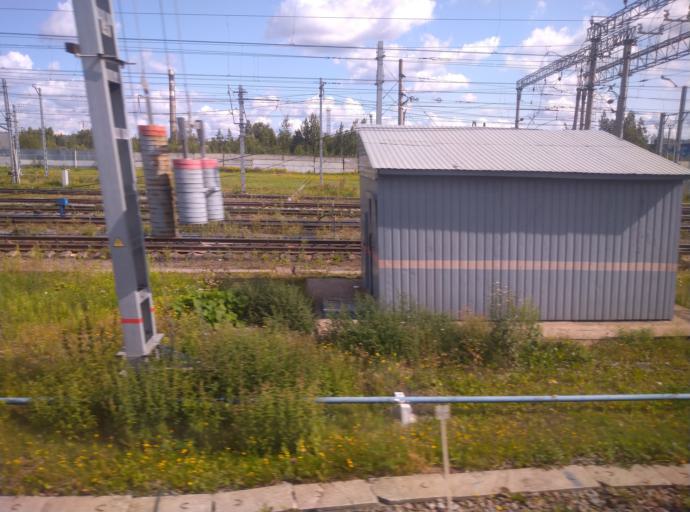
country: RU
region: St.-Petersburg
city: Obukhovo
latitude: 59.8512
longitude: 30.4507
